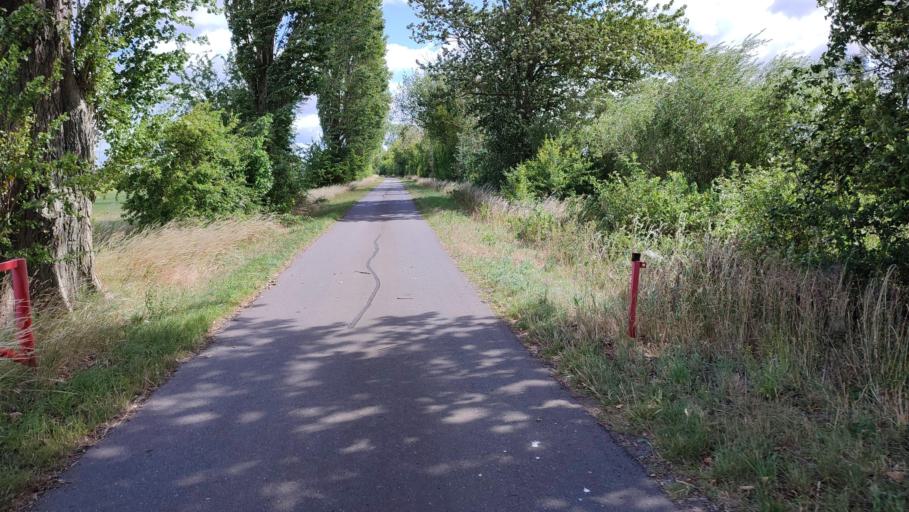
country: DE
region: Lower Saxony
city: Neu Darchau
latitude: 53.2165
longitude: 10.9650
